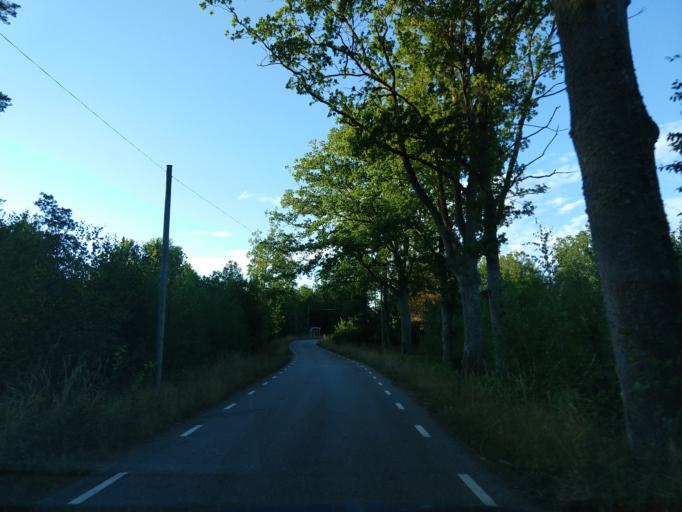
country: SE
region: Blekinge
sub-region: Ronneby Kommun
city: Brakne-Hoby
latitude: 56.2779
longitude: 15.1640
